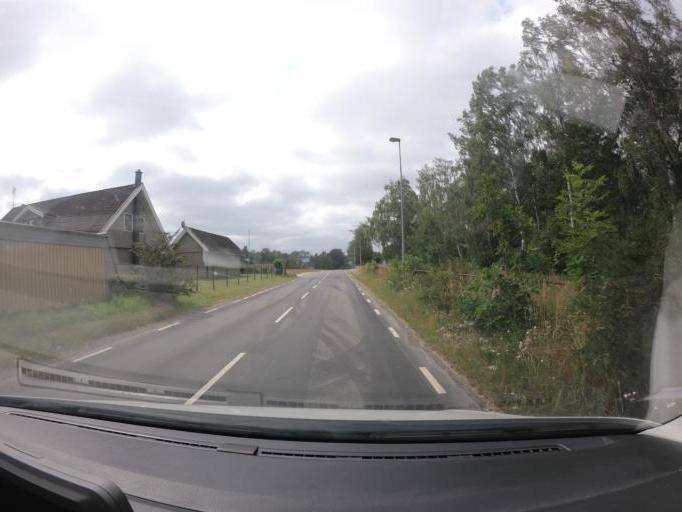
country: SE
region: Skane
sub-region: Hassleholms Kommun
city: Tormestorp
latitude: 56.1573
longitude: 13.6269
